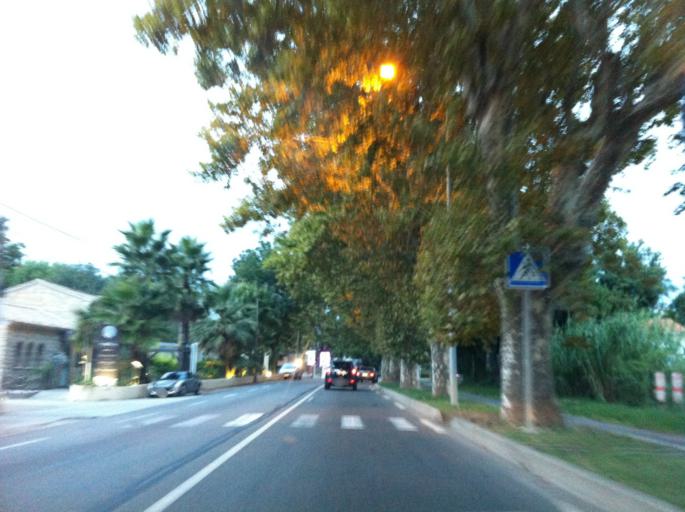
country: FR
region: Provence-Alpes-Cote d'Azur
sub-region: Departement du Var
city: Gassin
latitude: 43.2697
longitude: 6.5734
